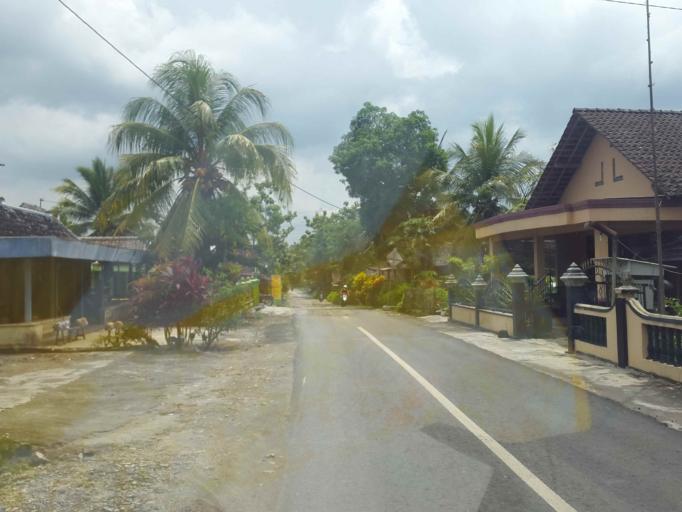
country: ID
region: Daerah Istimewa Yogyakarta
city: Wonosari
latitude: -7.9266
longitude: 110.6305
